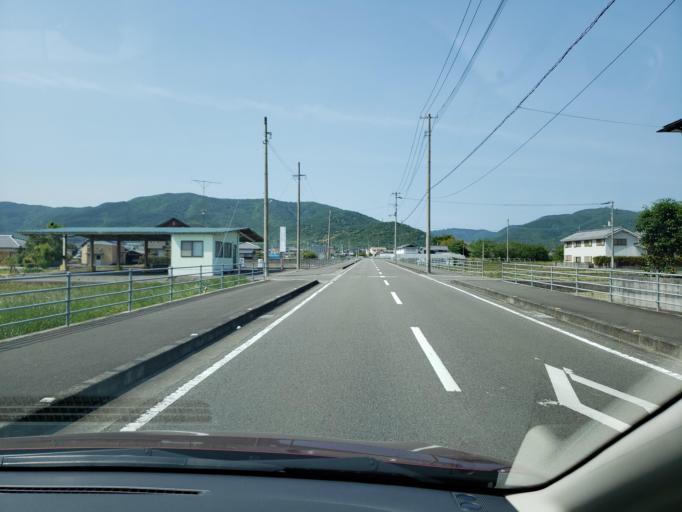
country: JP
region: Tokushima
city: Kamojimacho-jogejima
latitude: 34.1033
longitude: 134.3413
